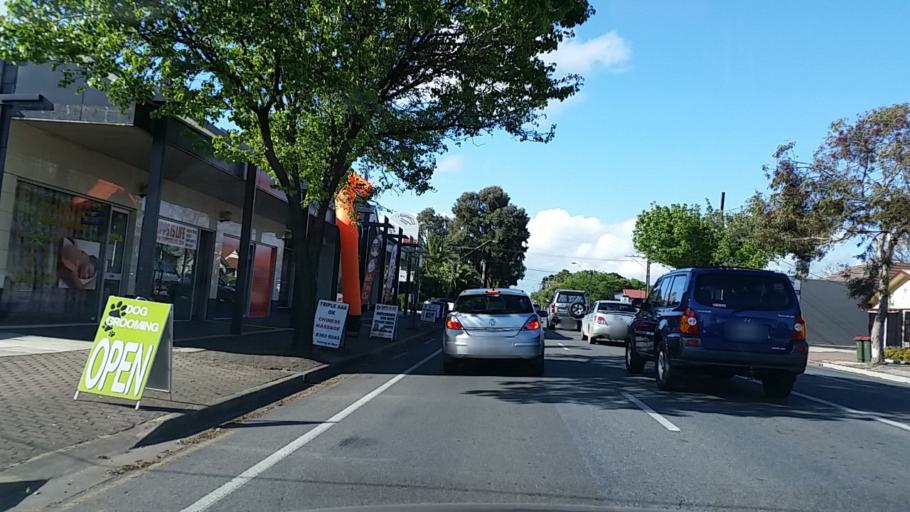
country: AU
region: South Australia
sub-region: Norwood Payneham St Peters
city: Royston Park
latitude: -34.9001
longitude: 138.6358
